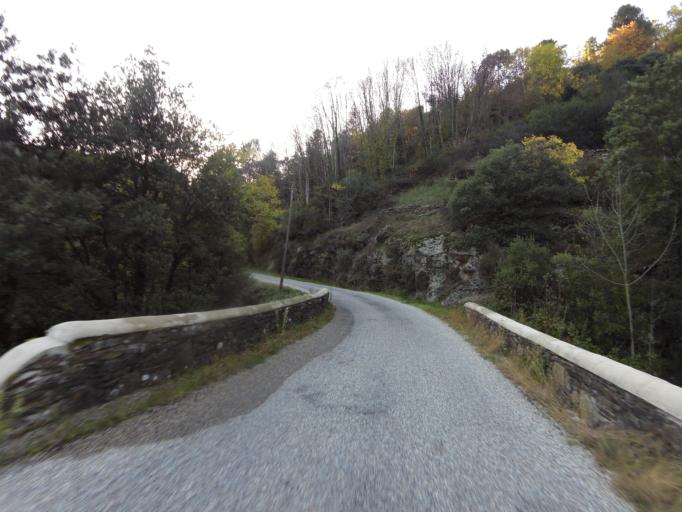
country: FR
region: Rhone-Alpes
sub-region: Departement de l'Ardeche
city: Lablachere
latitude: 44.5274
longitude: 4.1208
